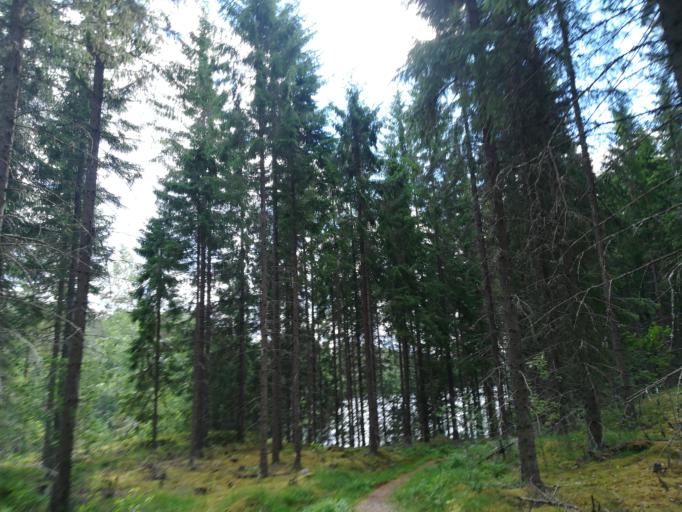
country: FI
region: Southern Savonia
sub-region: Mikkeli
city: Maentyharju
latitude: 61.3656
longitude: 26.9331
